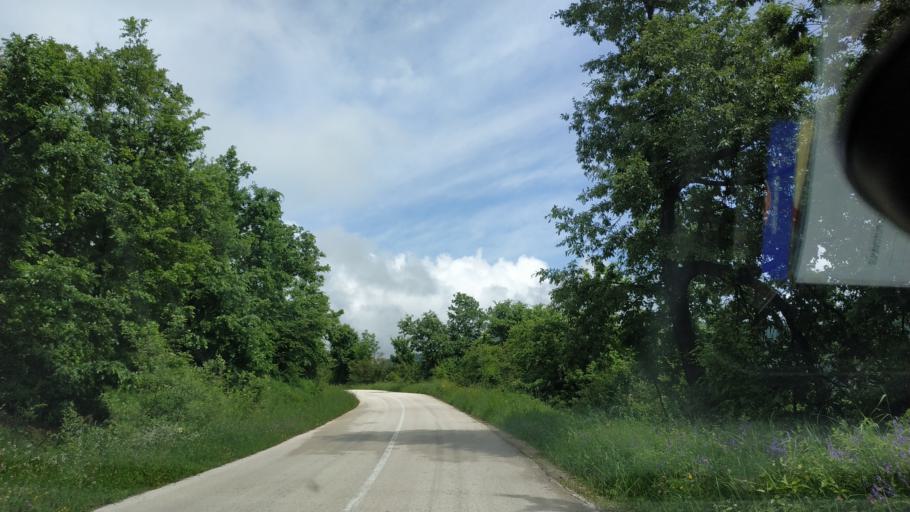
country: RS
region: Central Serbia
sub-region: Zajecarski Okrug
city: Boljevac
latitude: 43.7374
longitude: 21.9509
